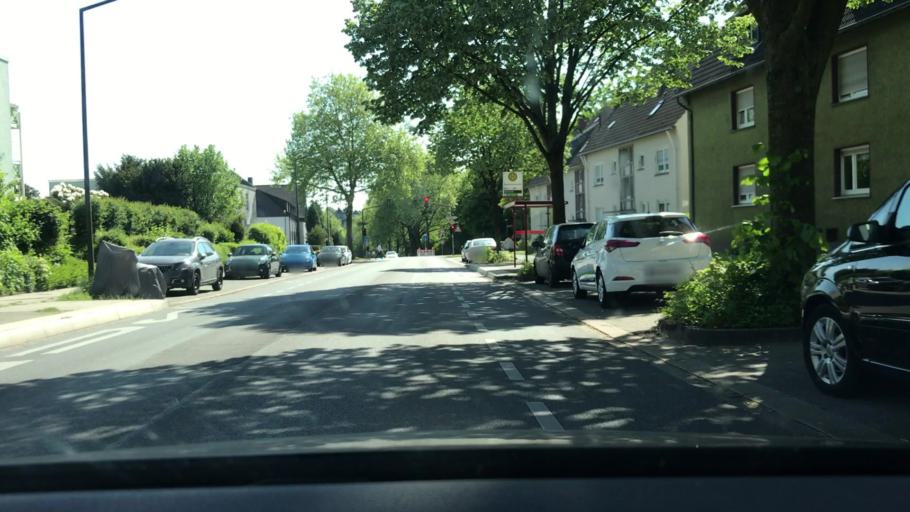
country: DE
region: North Rhine-Westphalia
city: Herten
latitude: 51.6043
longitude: 7.1429
